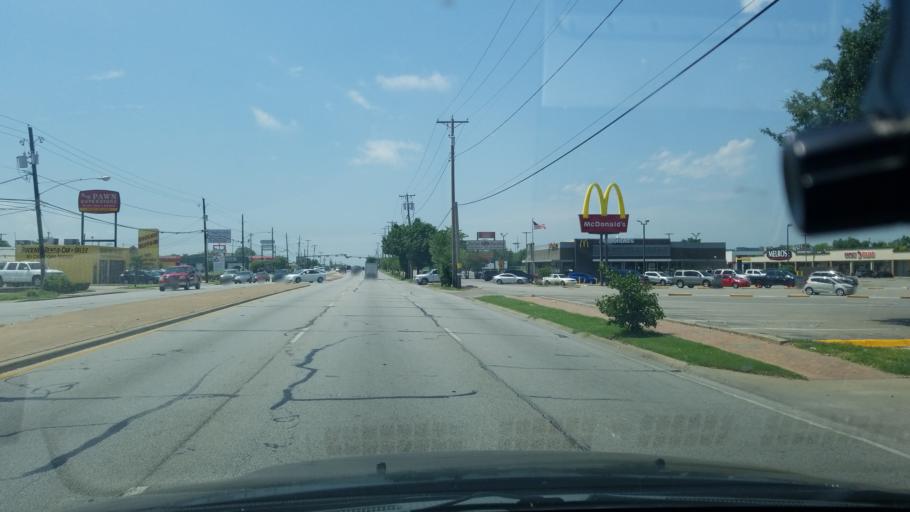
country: US
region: Texas
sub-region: Dallas County
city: Balch Springs
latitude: 32.7520
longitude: -96.6830
